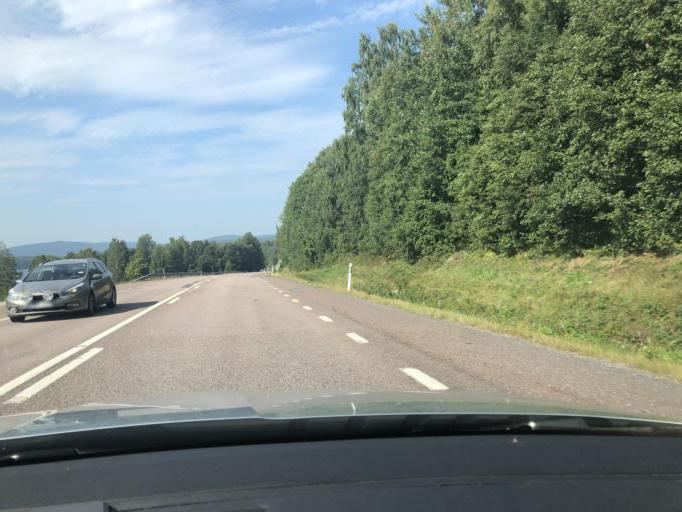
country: SE
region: Vaesternorrland
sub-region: Haernoesands Kommun
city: Haernoesand
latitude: 62.7949
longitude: 17.8905
